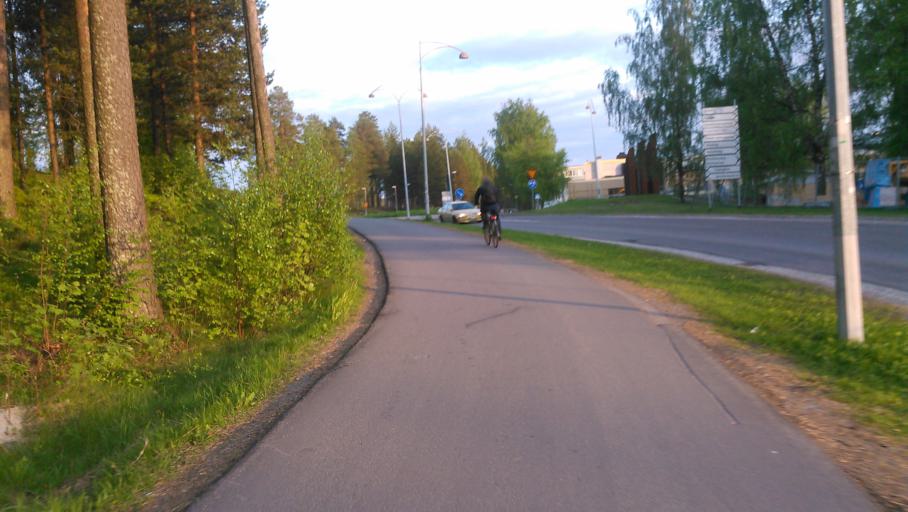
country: SE
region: Vaesterbotten
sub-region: Umea Kommun
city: Umea
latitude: 63.8189
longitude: 20.3039
